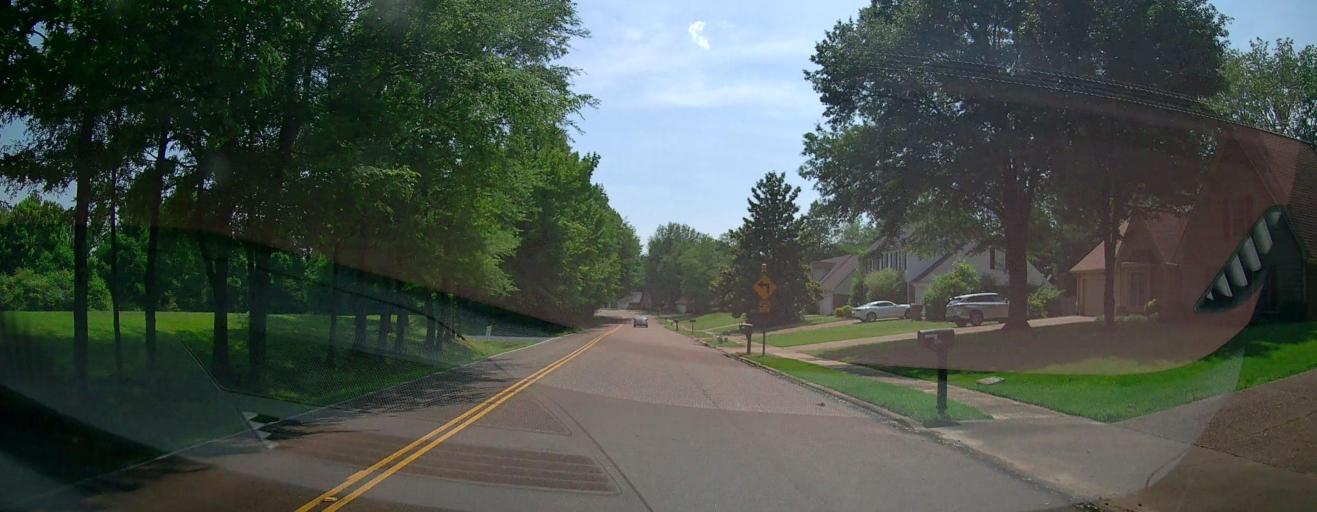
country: US
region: Mississippi
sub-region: De Soto County
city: Olive Branch
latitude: 35.0162
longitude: -89.8274
